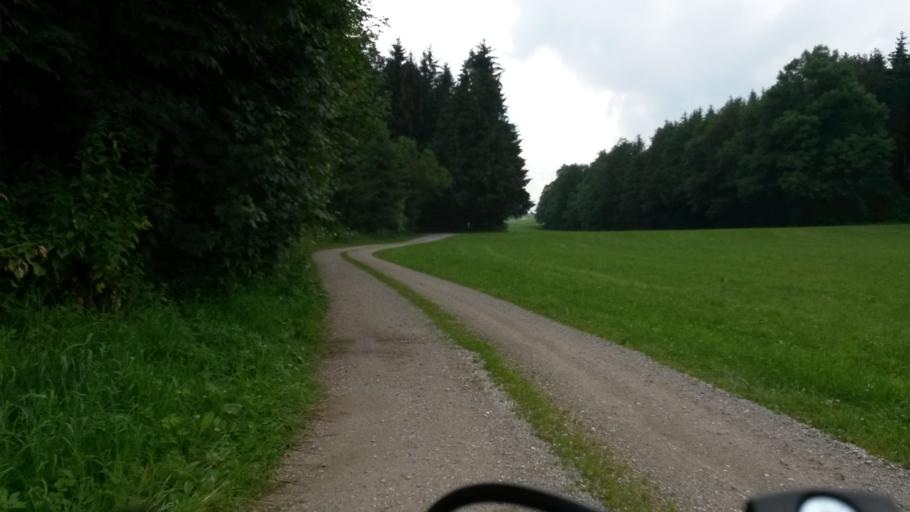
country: DE
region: Bavaria
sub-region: Upper Bavaria
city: Hoslwang
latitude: 47.9425
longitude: 12.3239
